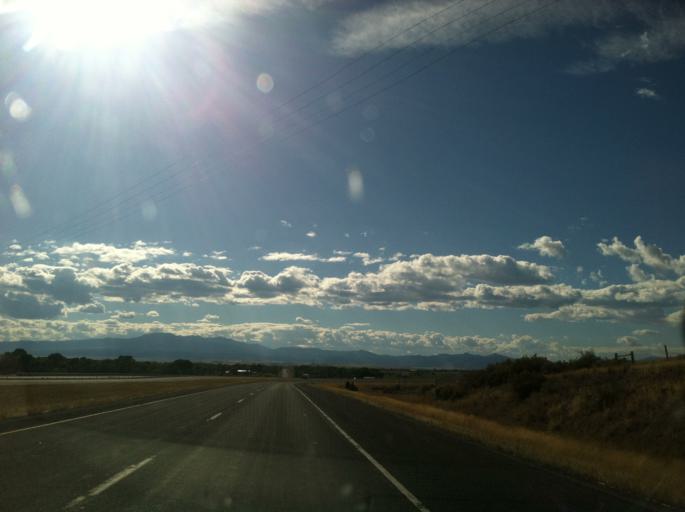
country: US
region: Montana
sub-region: Jefferson County
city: Whitehall
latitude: 45.8721
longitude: -112.0345
